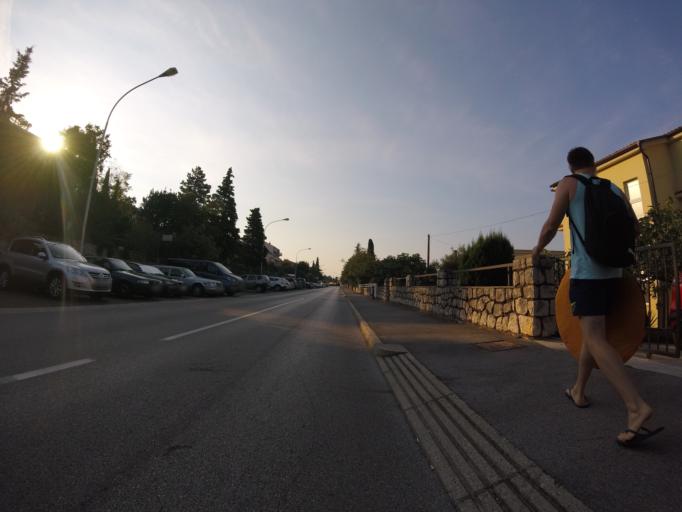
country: HR
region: Primorsko-Goranska
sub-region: Grad Crikvenica
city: Crikvenica
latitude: 45.1844
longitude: 14.6799
